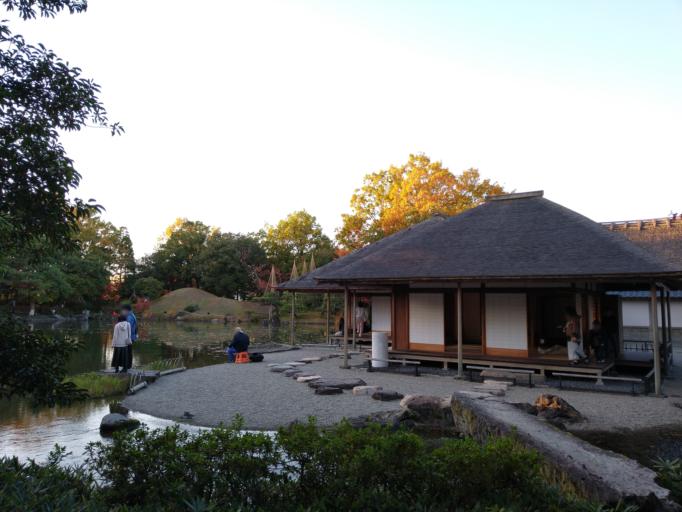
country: JP
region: Fukui
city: Fukui-shi
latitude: 36.0682
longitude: 136.2250
